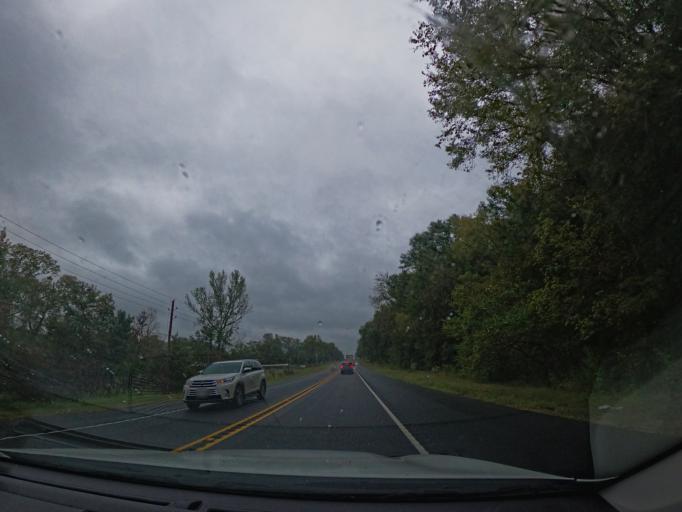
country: US
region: Louisiana
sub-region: Caddo Parish
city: Greenwood
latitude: 32.4262
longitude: -93.9850
